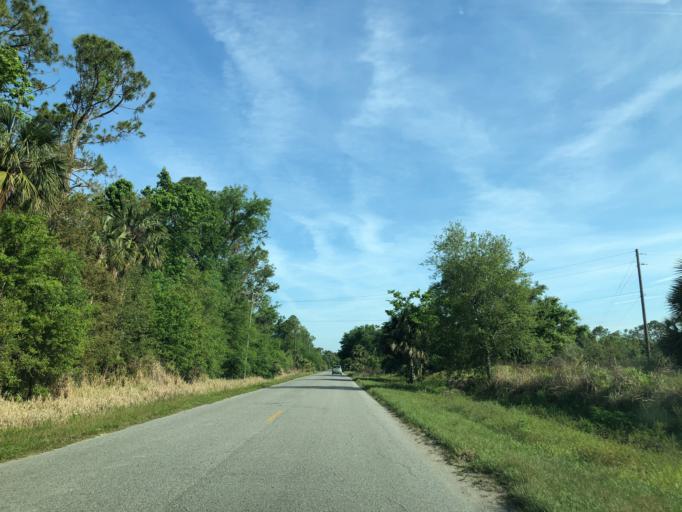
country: US
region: Florida
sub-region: Lake County
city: Astatula
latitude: 28.7086
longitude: -81.6731
